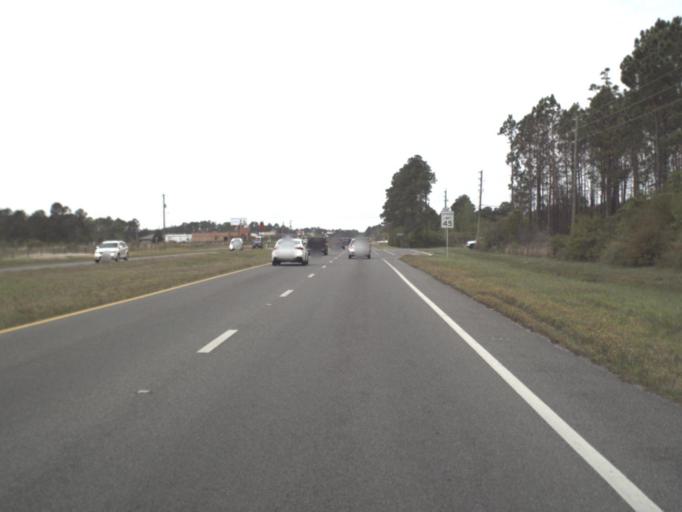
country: US
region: Florida
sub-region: Escambia County
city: Myrtle Grove
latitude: 30.4032
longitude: -87.3301
